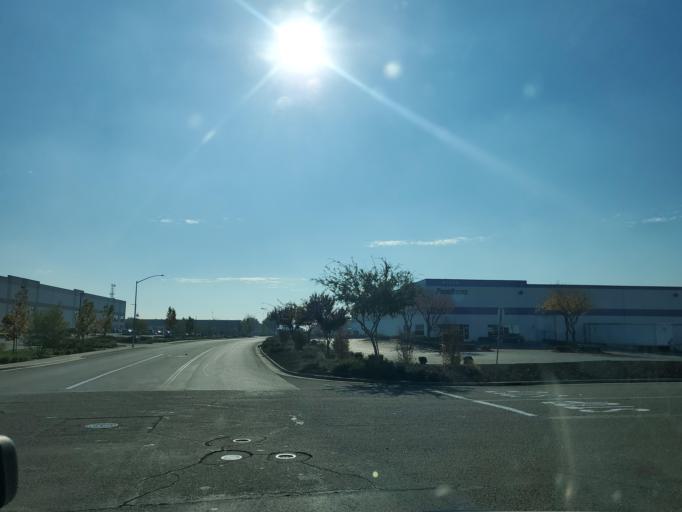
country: US
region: California
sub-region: San Joaquin County
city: Kennedy
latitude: 37.9091
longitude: -121.2453
